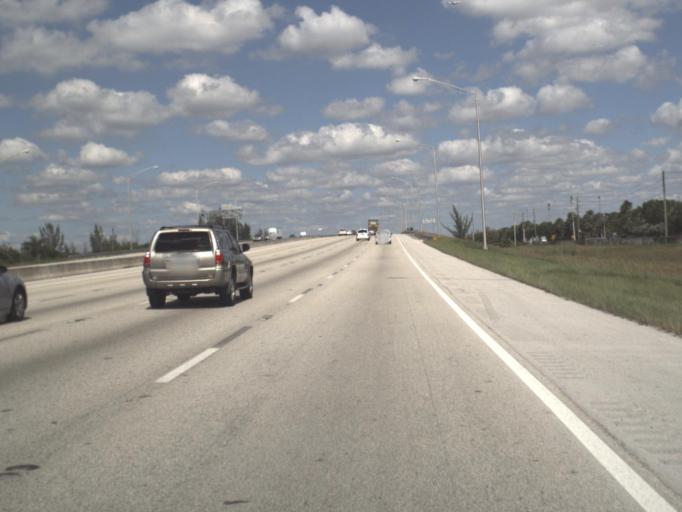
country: US
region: Florida
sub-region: Miami-Dade County
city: Doral
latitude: 25.8226
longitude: -80.3865
